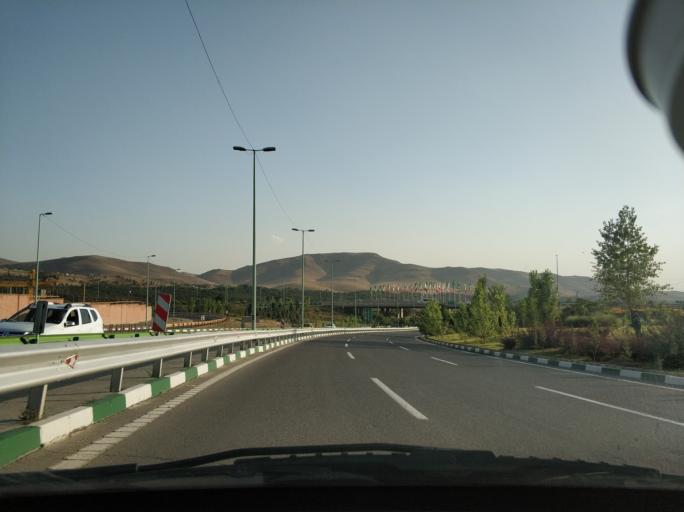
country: IR
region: Tehran
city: Tehran
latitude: 35.7256
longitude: 51.5881
